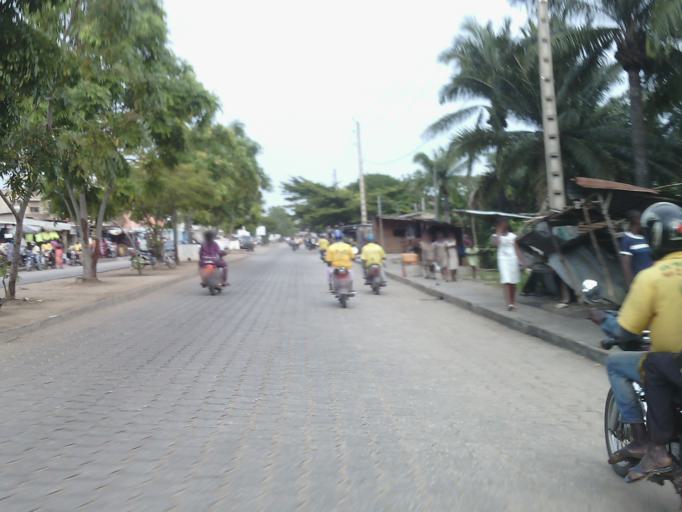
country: BJ
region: Littoral
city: Cotonou
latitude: 6.3901
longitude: 2.3715
